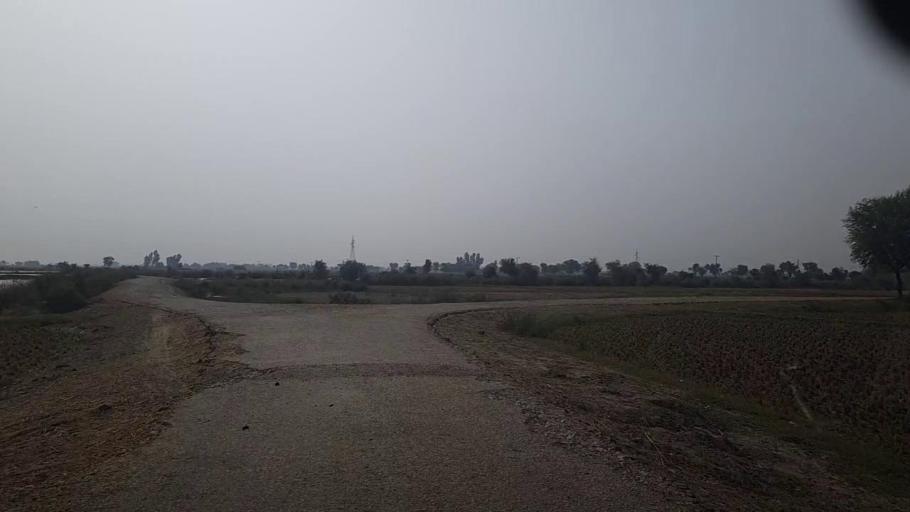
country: PK
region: Sindh
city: Kashmor
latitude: 28.3962
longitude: 69.4205
